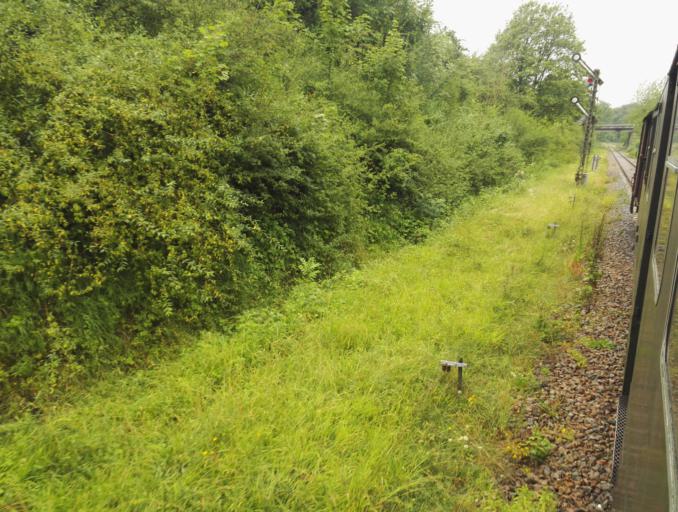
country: DE
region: Baden-Wuerttemberg
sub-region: Freiburg Region
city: Blumberg
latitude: 47.8253
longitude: 8.5479
